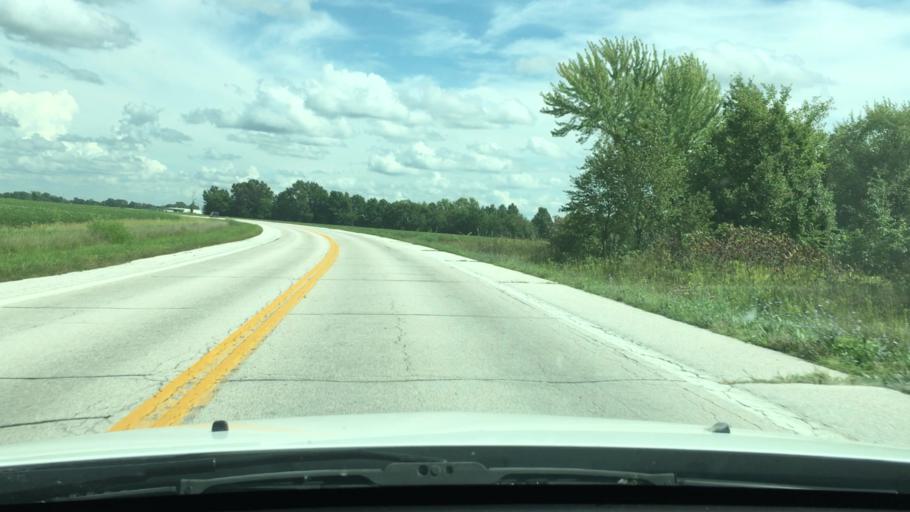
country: US
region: Missouri
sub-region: Audrain County
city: Vandalia
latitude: 39.3377
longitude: -91.4216
